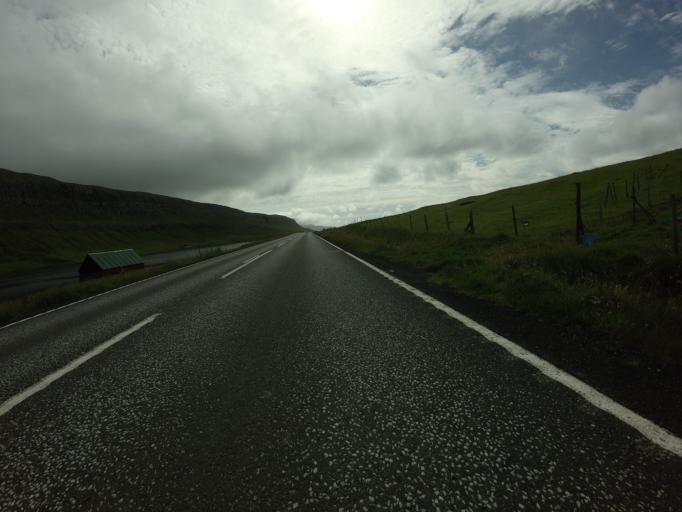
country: FO
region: Sandoy
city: Sandur
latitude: 61.8551
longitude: -6.8288
